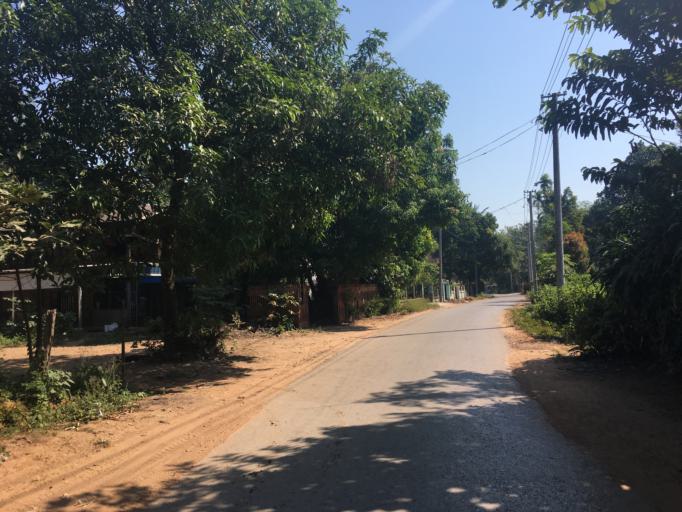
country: MM
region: Mon
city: Mawlamyine
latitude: 16.4322
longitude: 97.6980
